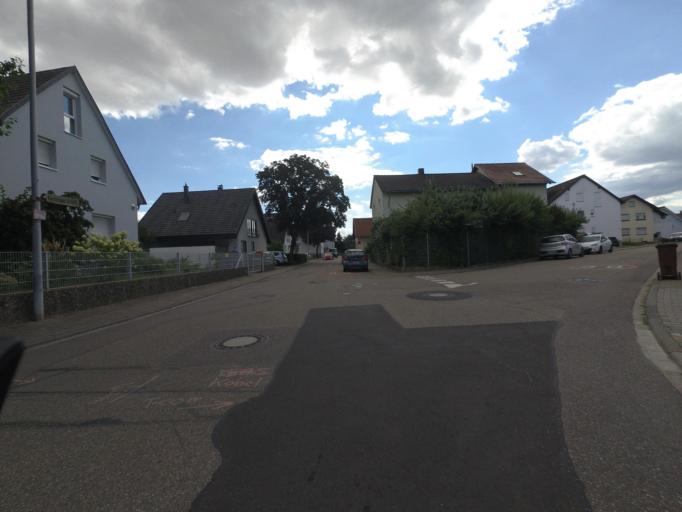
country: DE
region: Baden-Wuerttemberg
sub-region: Karlsruhe Region
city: Sinzheim
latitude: 48.7751
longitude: 8.1718
